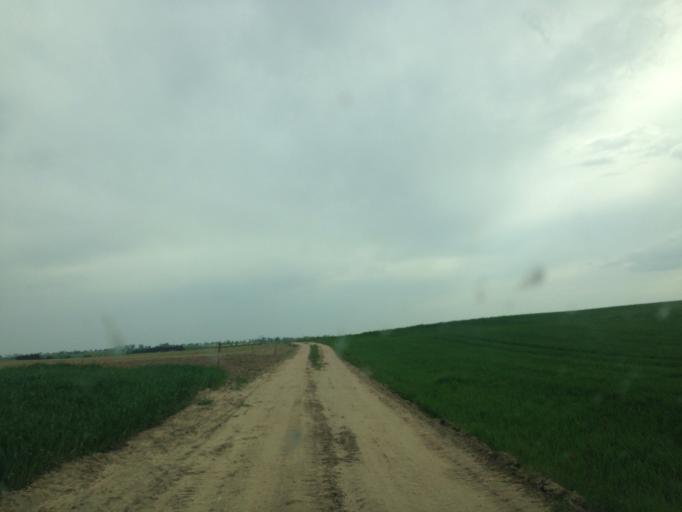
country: PL
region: Kujawsko-Pomorskie
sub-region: Powiat brodnicki
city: Bartniczka
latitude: 53.2626
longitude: 19.6232
